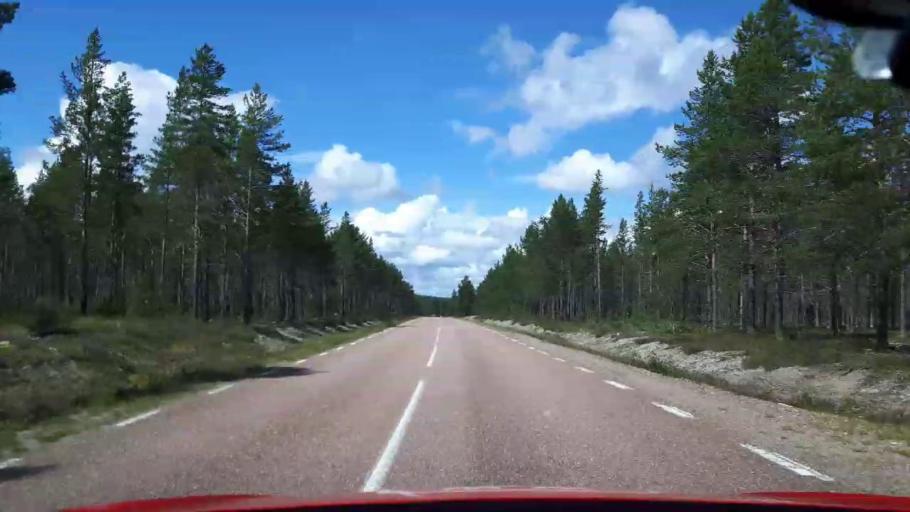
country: SE
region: Dalarna
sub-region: Alvdalens Kommun
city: AElvdalen
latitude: 61.8193
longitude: 13.5793
